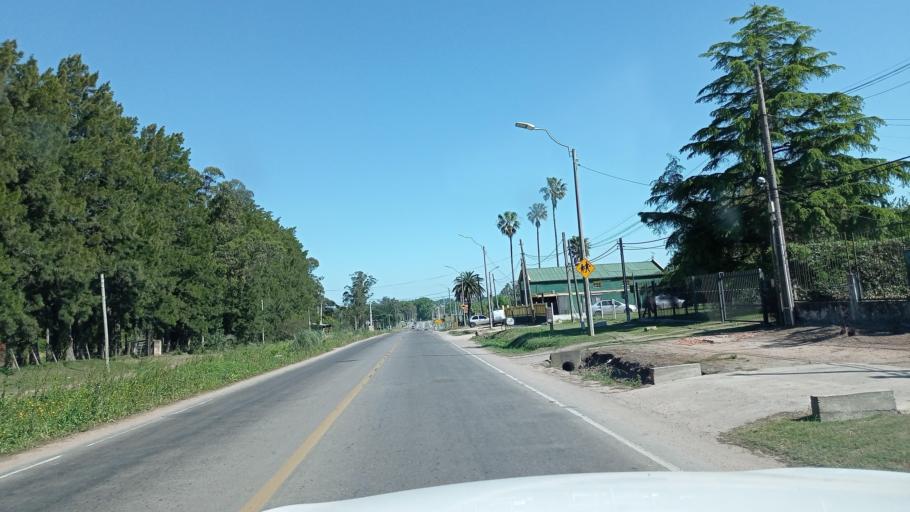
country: UY
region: Canelones
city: La Paz
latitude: -34.7913
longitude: -56.1655
